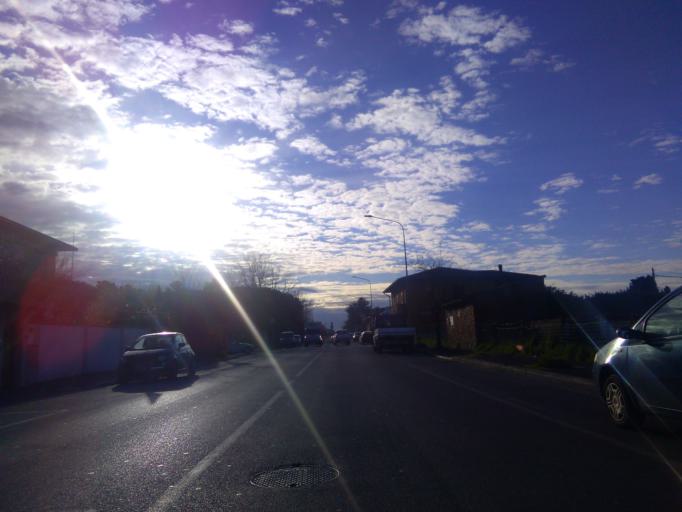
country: IT
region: Tuscany
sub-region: Provincia di Massa-Carrara
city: Marina di Carrara
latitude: 44.0529
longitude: 10.0435
